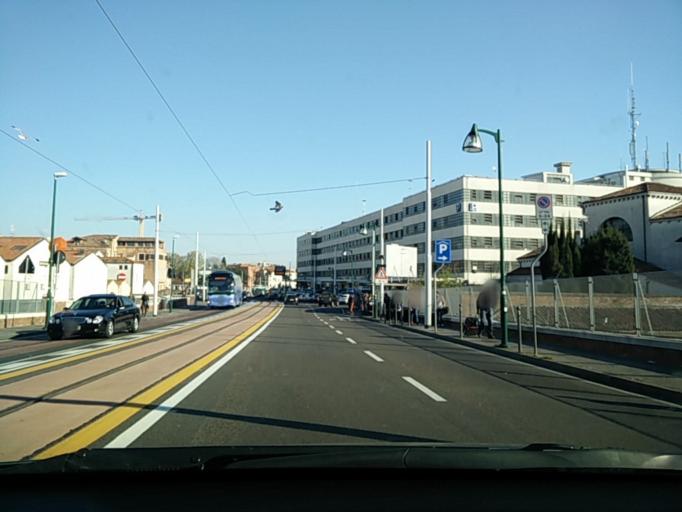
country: IT
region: Veneto
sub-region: Provincia di Venezia
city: Venice
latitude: 45.4397
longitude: 12.3166
